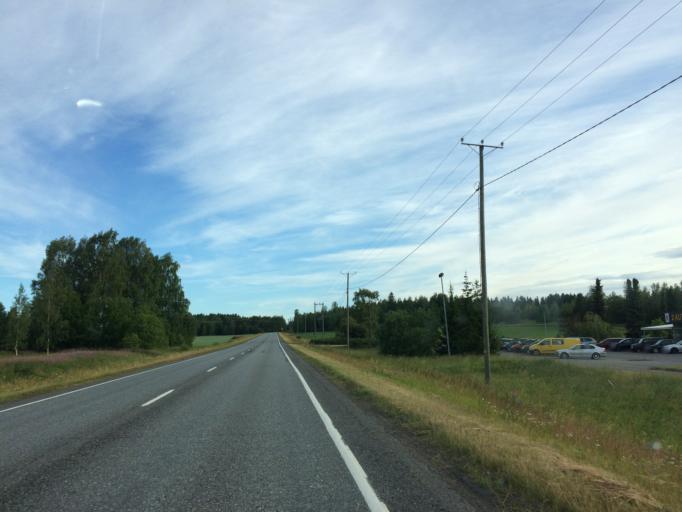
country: FI
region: Haeme
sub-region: Haemeenlinna
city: Janakkala
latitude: 60.9021
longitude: 24.5566
